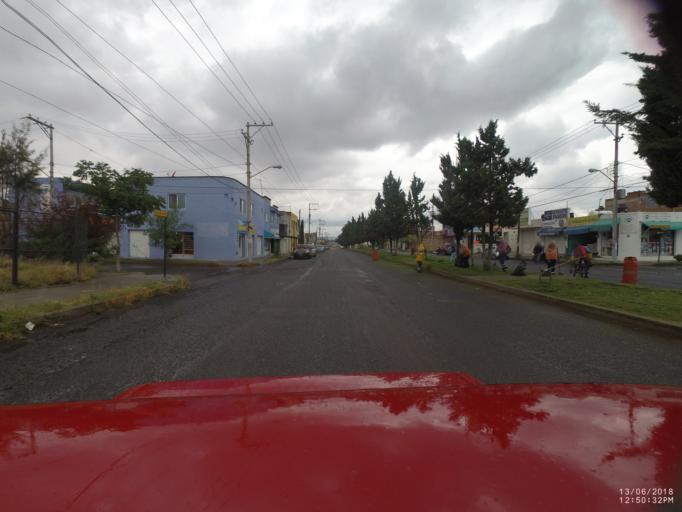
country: MX
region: Aguascalientes
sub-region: Jesus Maria
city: Arboledas Paso Blanco [Fraccionamiento]
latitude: 21.9687
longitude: -102.2994
